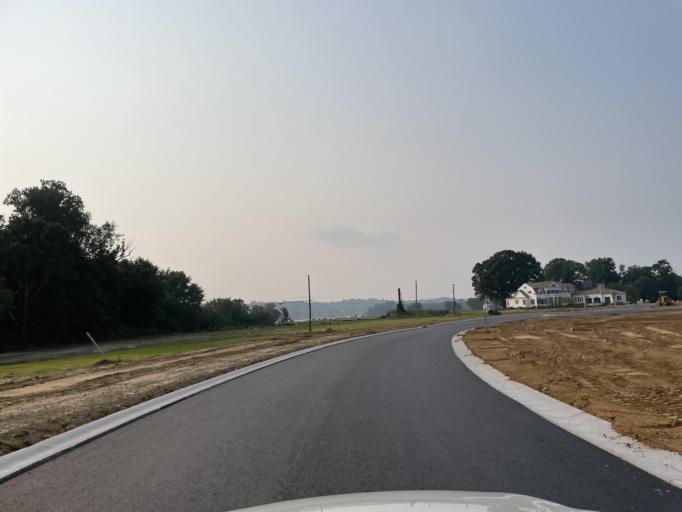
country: US
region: Kentucky
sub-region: Jefferson County
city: Prospect
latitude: 38.3563
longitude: -85.6260
